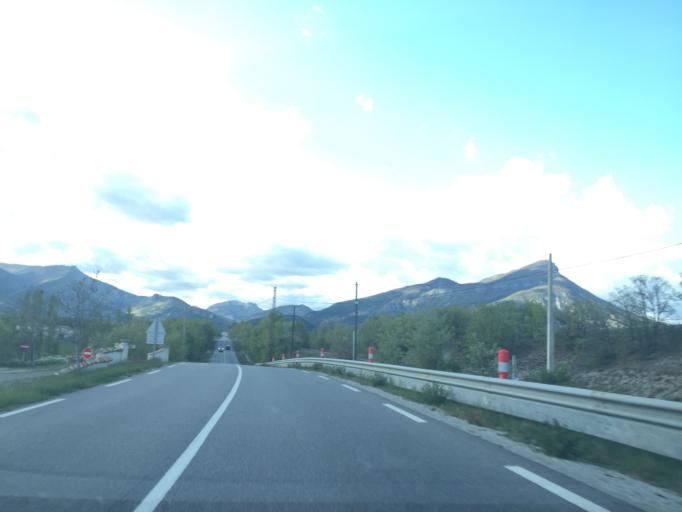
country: FR
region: Provence-Alpes-Cote d'Azur
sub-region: Departement des Hautes-Alpes
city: Serres
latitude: 44.3871
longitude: 5.7436
